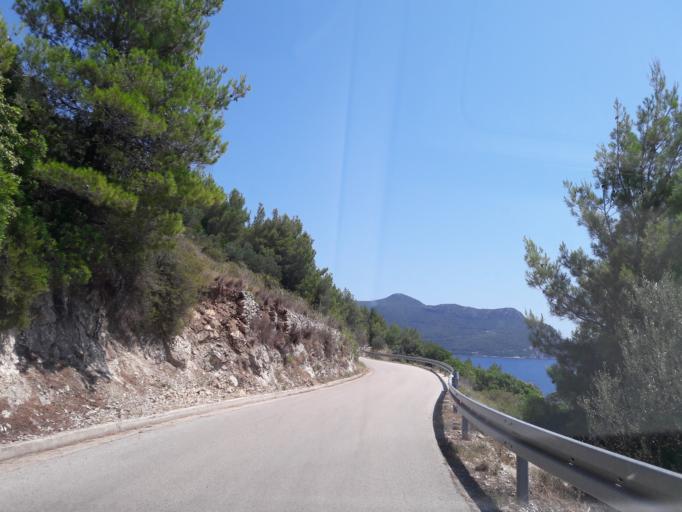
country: HR
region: Dubrovacko-Neretvanska
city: Blato
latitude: 42.9081
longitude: 17.4224
